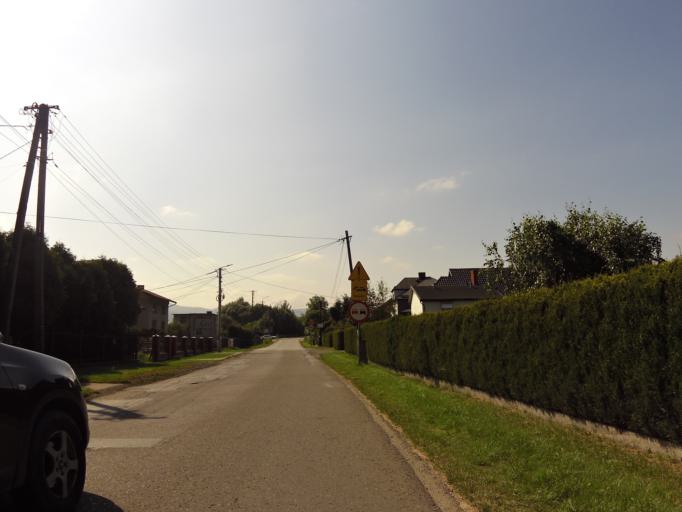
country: PL
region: Silesian Voivodeship
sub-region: Powiat zywiecki
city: Wieprz
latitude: 49.6474
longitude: 19.1775
